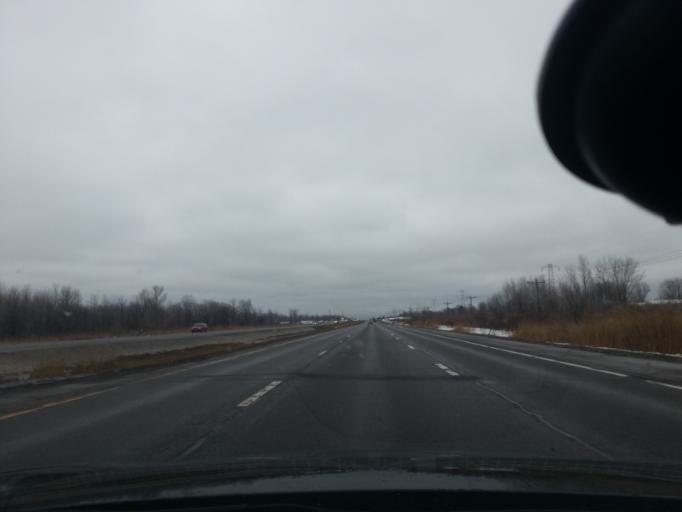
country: US
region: New York
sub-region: Onondaga County
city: Brewerton
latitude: 43.2080
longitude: -76.1283
